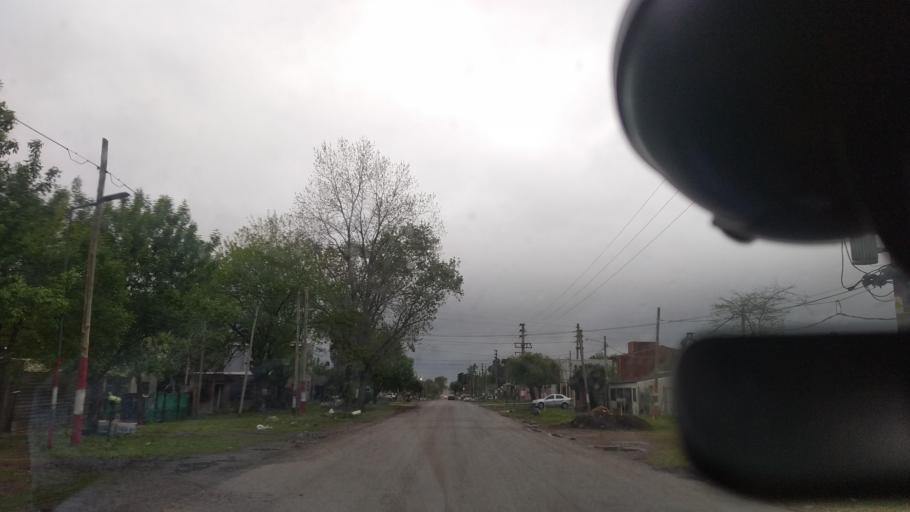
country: AR
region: Buenos Aires
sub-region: Partido de La Plata
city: La Plata
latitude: -34.9531
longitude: -57.9953
